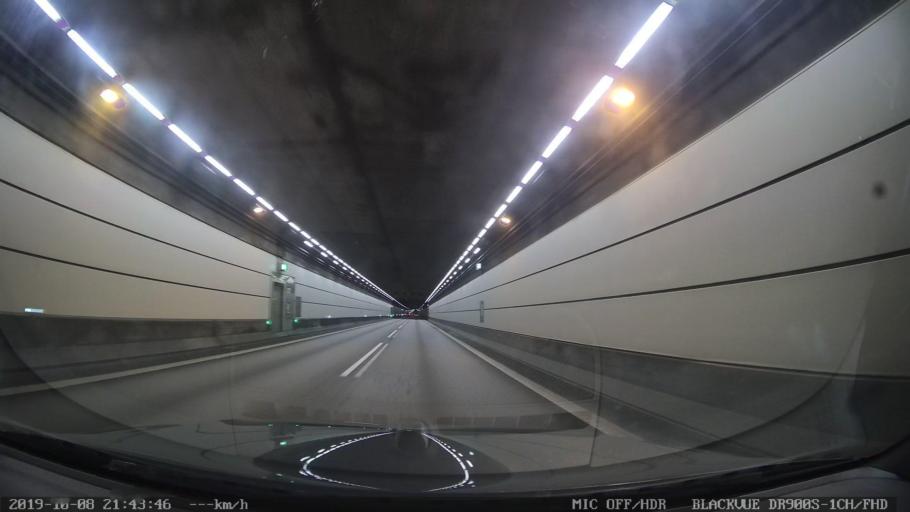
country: DK
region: Capital Region
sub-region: Dragor Kommune
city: Dragor
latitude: 55.6119
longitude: 12.7261
